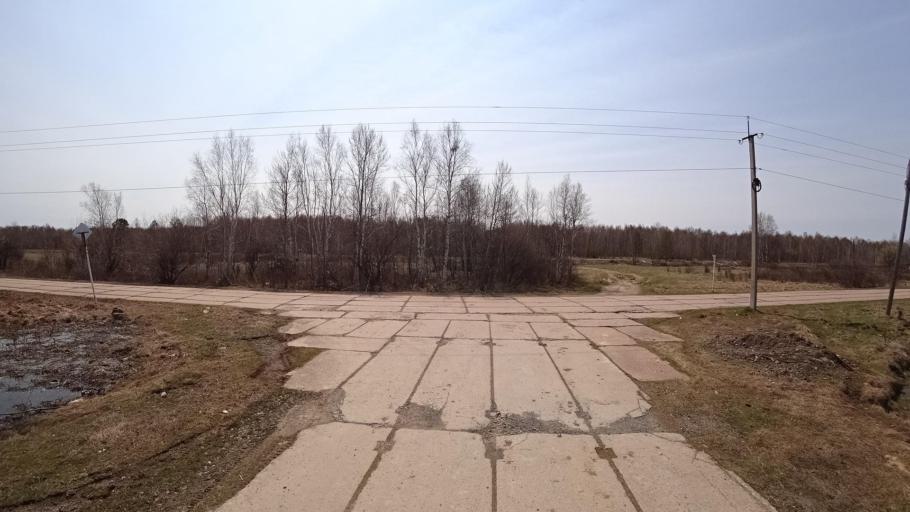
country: RU
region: Khabarovsk Krai
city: Selikhino
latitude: 50.3845
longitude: 137.3733
